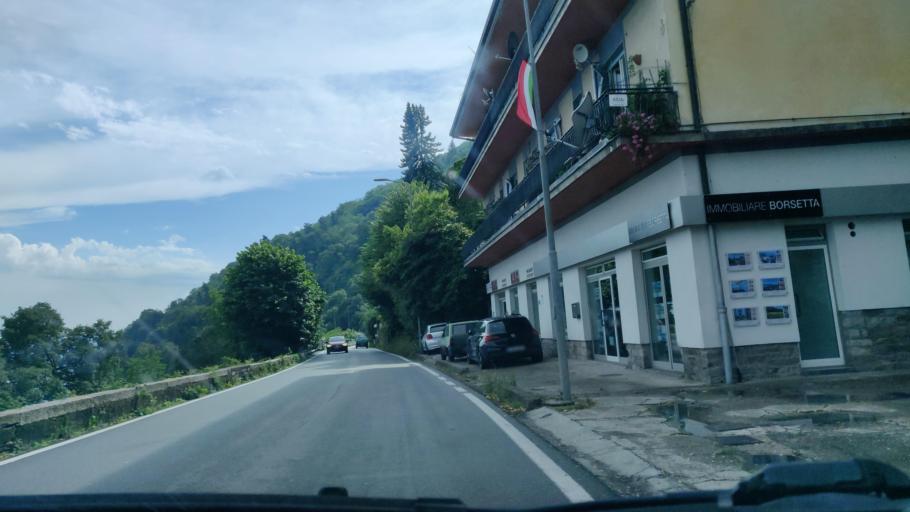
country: IT
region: Piedmont
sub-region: Provincia Verbano-Cusio-Ossola
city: Cannero Riviera
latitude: 46.0207
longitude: 8.6752
